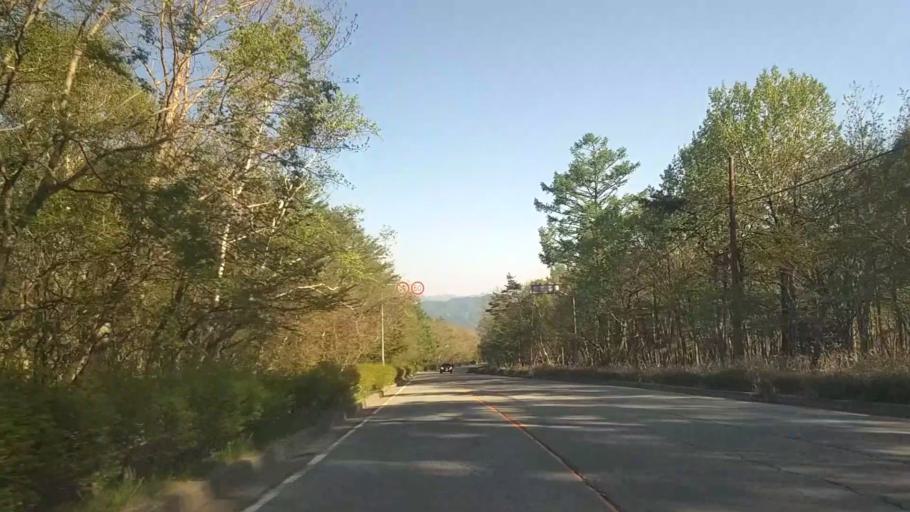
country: JP
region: Yamanashi
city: Nirasaki
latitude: 35.9324
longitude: 138.4263
